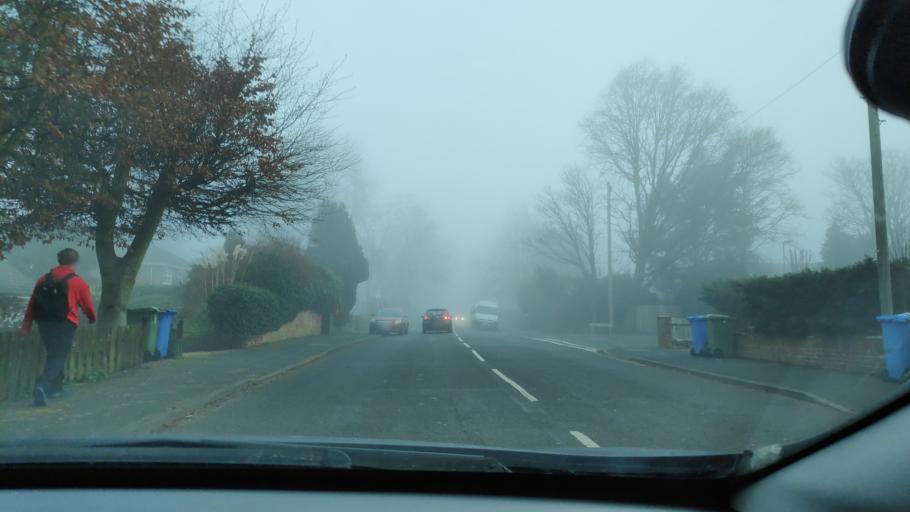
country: GB
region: England
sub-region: Hampshire
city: Farnborough
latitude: 51.2883
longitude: -0.7452
